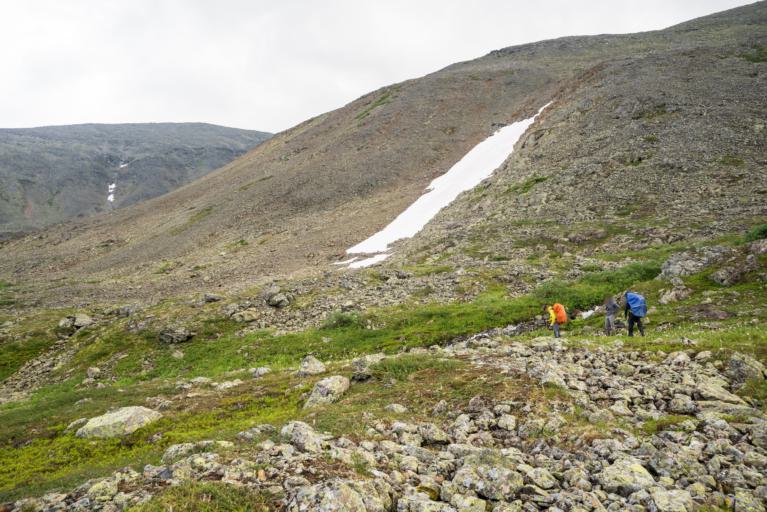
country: RU
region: Komi Republic
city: Synya
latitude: 64.8203
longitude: 59.2515
